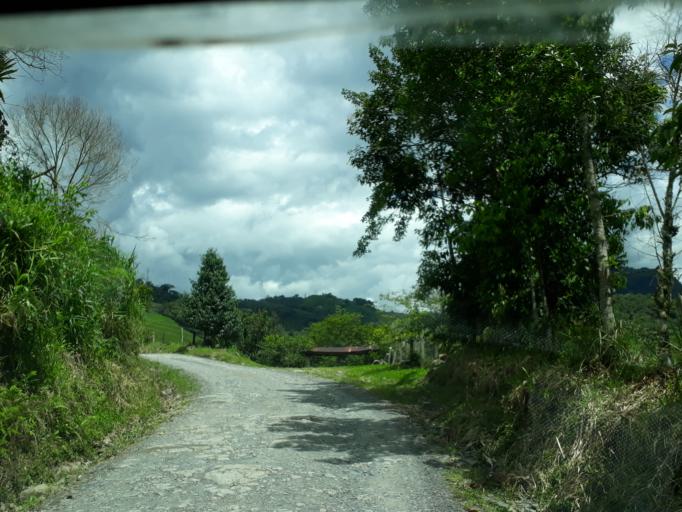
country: CO
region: Cundinamarca
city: Topaipi
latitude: 5.3463
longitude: -74.1909
